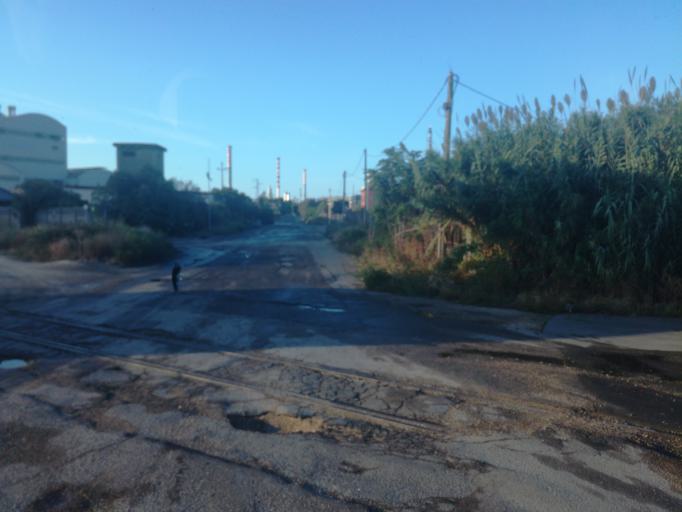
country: IT
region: Apulia
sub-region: Provincia di Taranto
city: Statte
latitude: 40.5019
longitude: 17.1993
